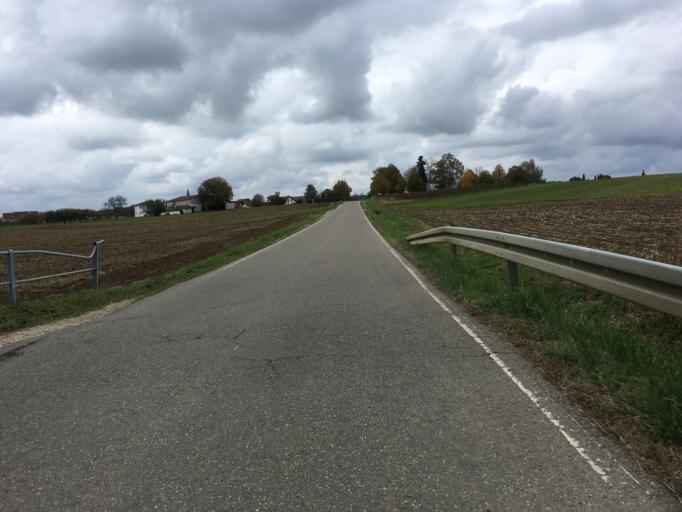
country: DE
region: Baden-Wuerttemberg
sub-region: Tuebingen Region
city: Gomaringen
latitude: 48.4786
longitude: 9.1098
